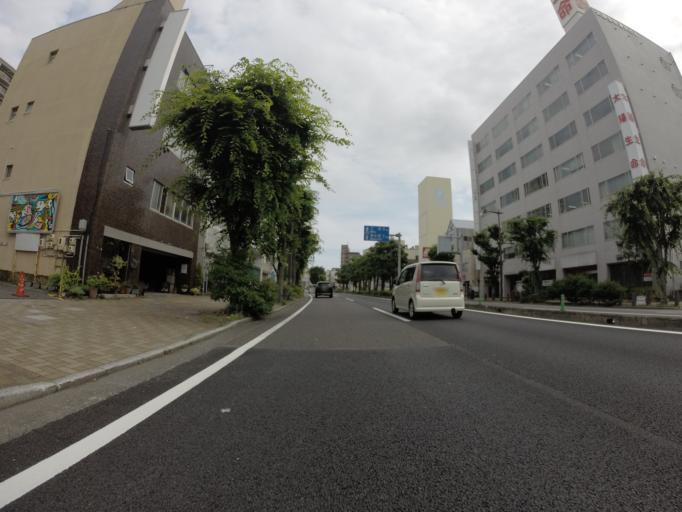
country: JP
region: Shizuoka
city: Shizuoka-shi
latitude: 35.0221
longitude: 138.4871
